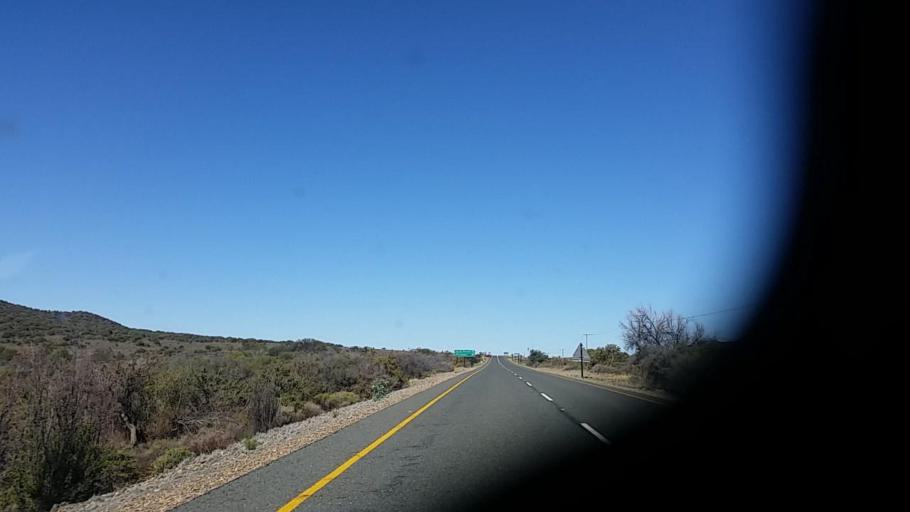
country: ZA
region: Eastern Cape
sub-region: Cacadu District Municipality
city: Willowmore
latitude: -33.4754
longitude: 23.0935
